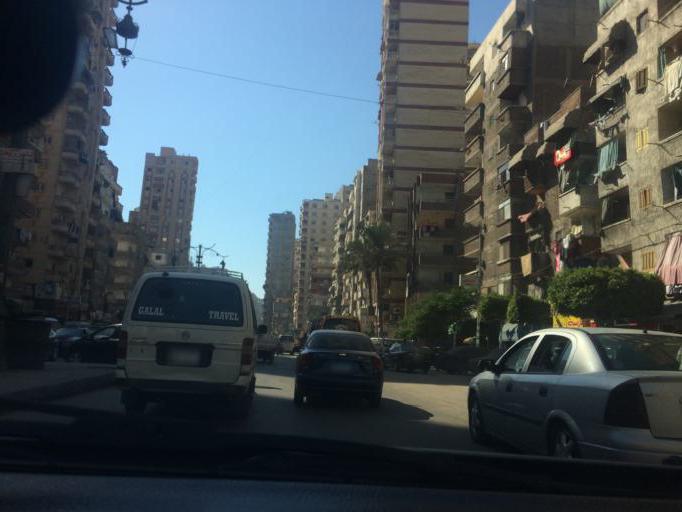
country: EG
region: Alexandria
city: Alexandria
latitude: 31.2642
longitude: 30.0055
